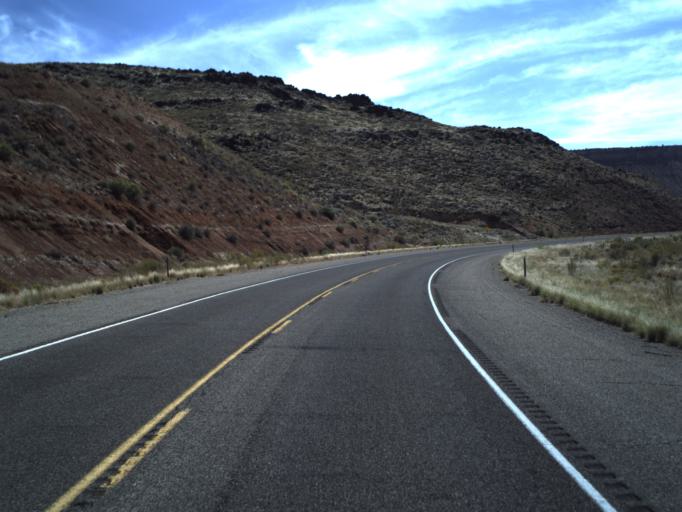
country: US
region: Utah
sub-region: Washington County
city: LaVerkin
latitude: 37.1782
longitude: -113.1167
